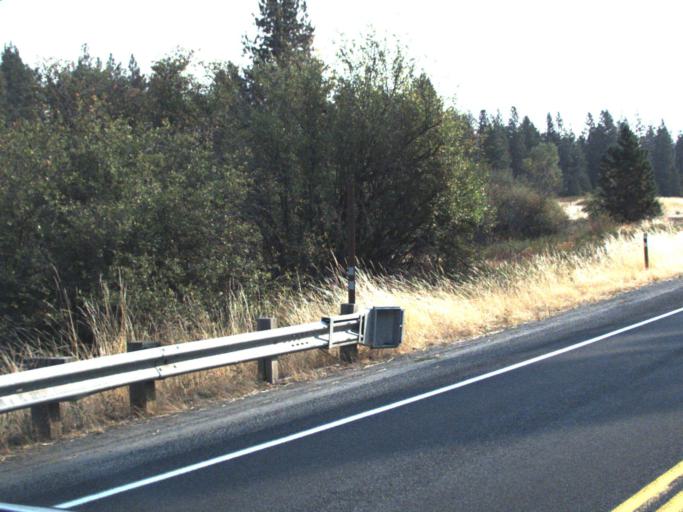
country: US
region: Washington
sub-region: Spokane County
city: Veradale
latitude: 47.4441
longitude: -117.1233
